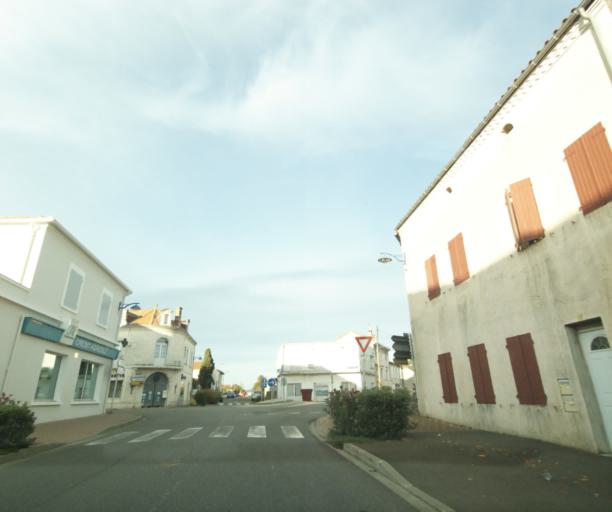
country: FR
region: Aquitaine
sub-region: Departement des Landes
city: Gabarret
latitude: 43.9855
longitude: 0.0094
